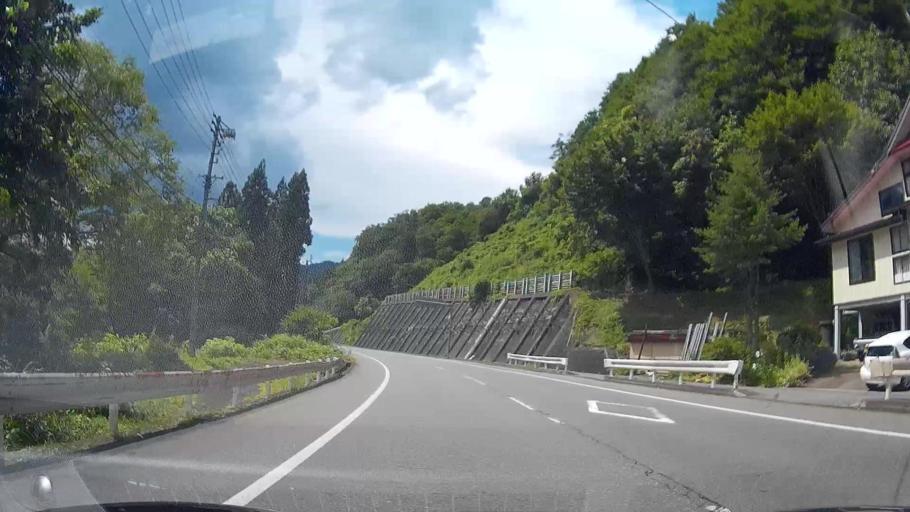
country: JP
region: Niigata
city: Tokamachi
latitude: 36.9910
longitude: 138.5734
